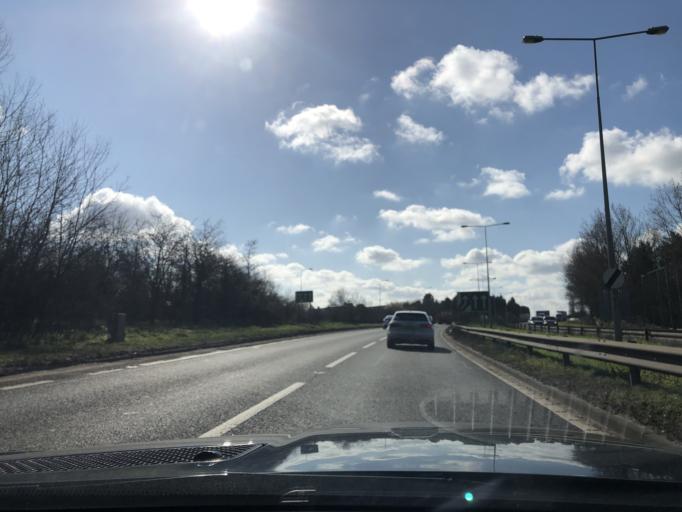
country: GB
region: England
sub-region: Northamptonshire
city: Hardingstone
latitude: 52.1930
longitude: -0.8922
